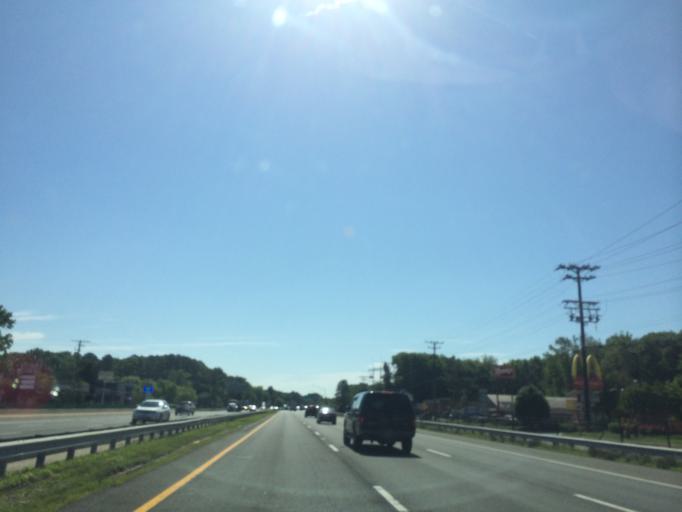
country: US
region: Maryland
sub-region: Anne Arundel County
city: Cape Saint Claire
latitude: 39.0266
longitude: -76.4451
